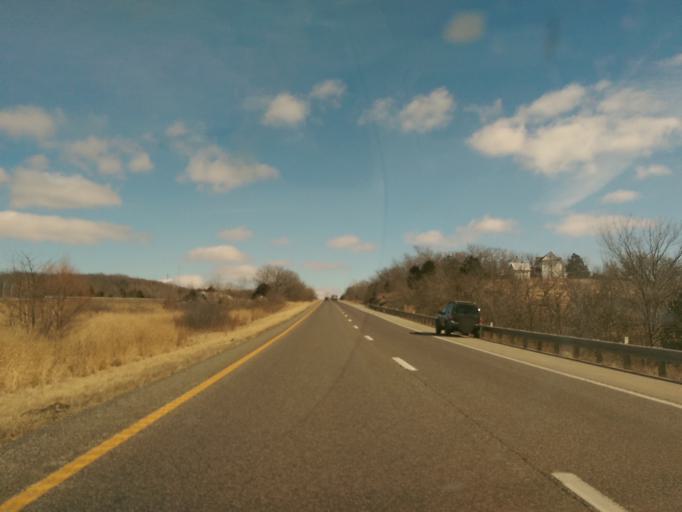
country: US
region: Missouri
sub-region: Montgomery County
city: Montgomery City
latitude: 38.9006
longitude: -91.5784
